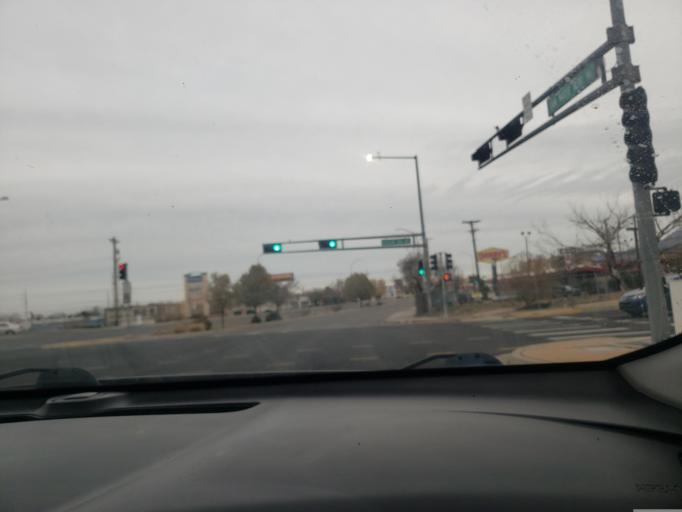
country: US
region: New Mexico
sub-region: Bernalillo County
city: Albuquerque
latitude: 35.1053
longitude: -106.5878
